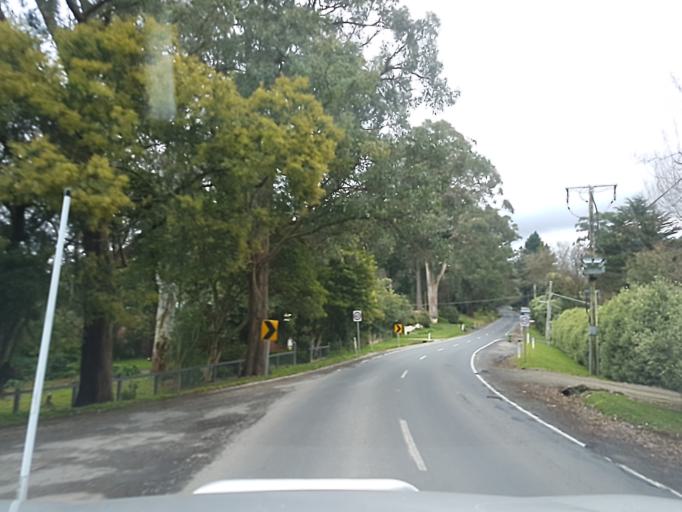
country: AU
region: Victoria
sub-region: Yarra Ranges
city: Monbulk
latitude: -37.8988
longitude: 145.3917
